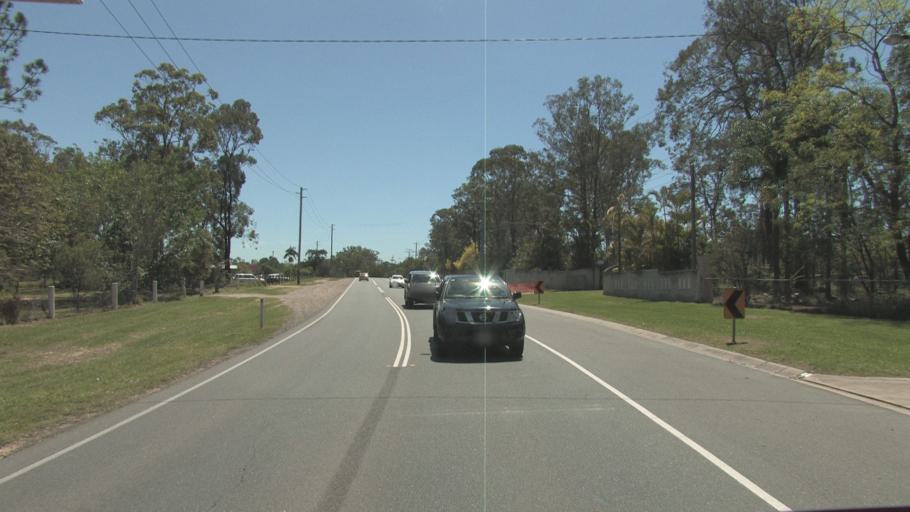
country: AU
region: Queensland
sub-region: Logan
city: Park Ridge South
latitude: -27.7040
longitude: 153.0088
